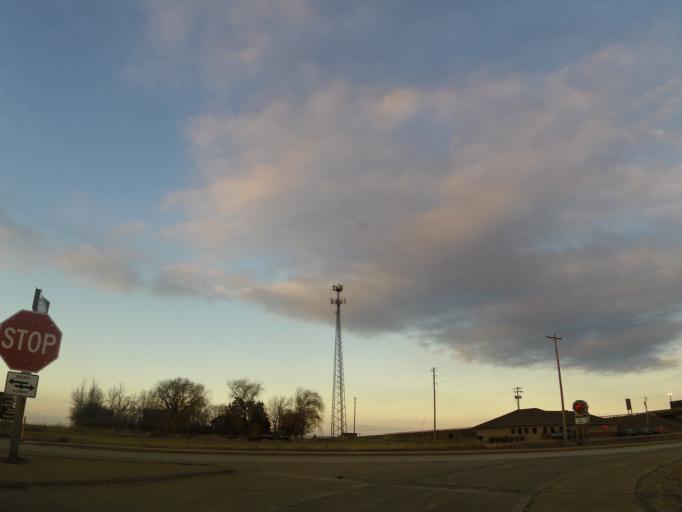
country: US
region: Illinois
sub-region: Woodford County
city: El Paso
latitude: 40.7366
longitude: -89.0370
